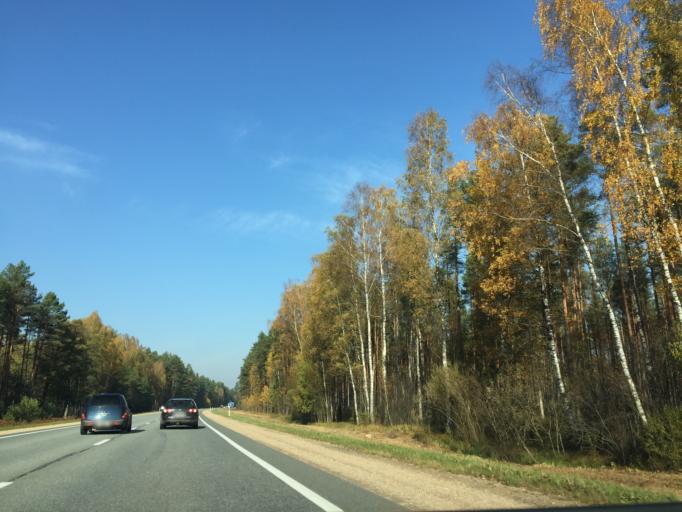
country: LV
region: Babite
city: Pinki
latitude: 56.9088
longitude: 23.9169
